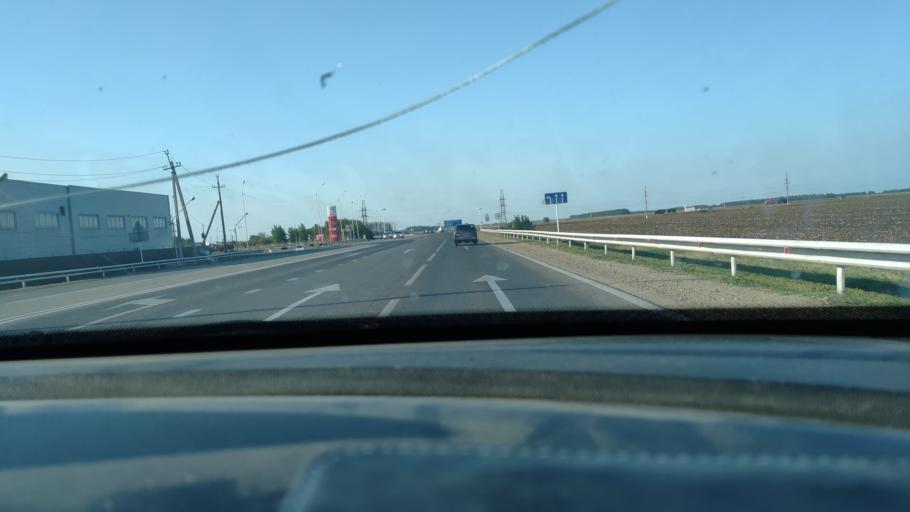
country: RU
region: Krasnodarskiy
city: Timashevsk
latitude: 45.6220
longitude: 38.9862
